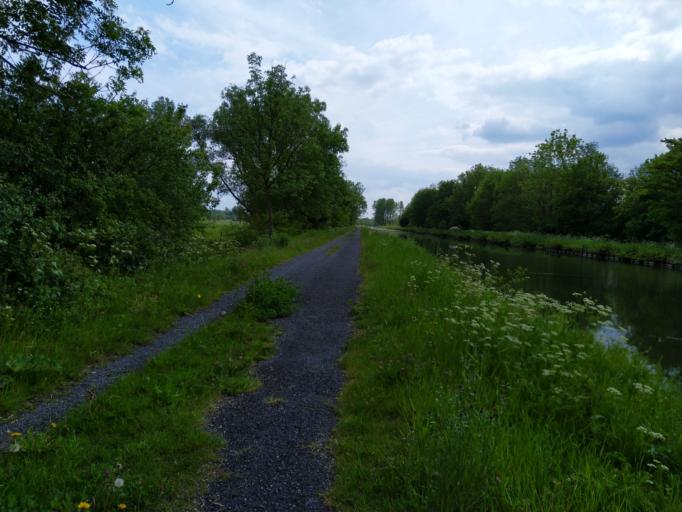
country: FR
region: Nord-Pas-de-Calais
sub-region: Departement du Nord
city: Landrecies
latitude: 50.0709
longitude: 3.6480
